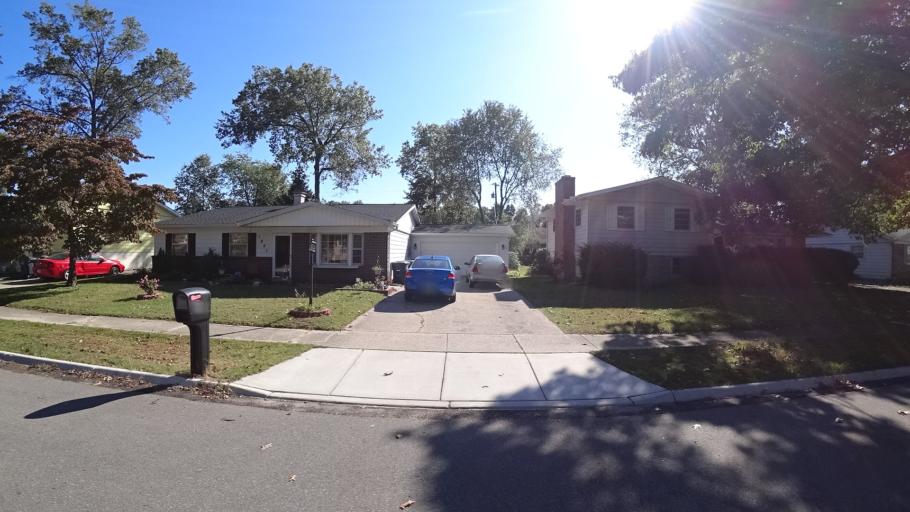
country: US
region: Indiana
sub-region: LaPorte County
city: Michigan City
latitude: 41.6880
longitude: -86.9068
